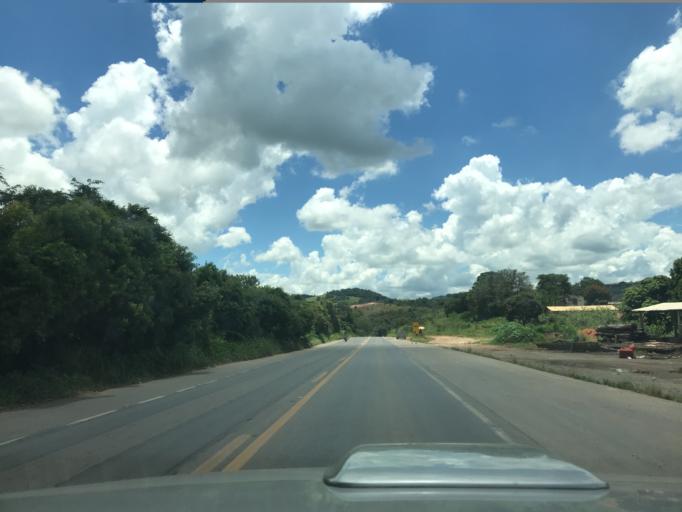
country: BR
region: Minas Gerais
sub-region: Perdoes
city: Perdoes
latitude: -21.1001
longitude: -45.0983
